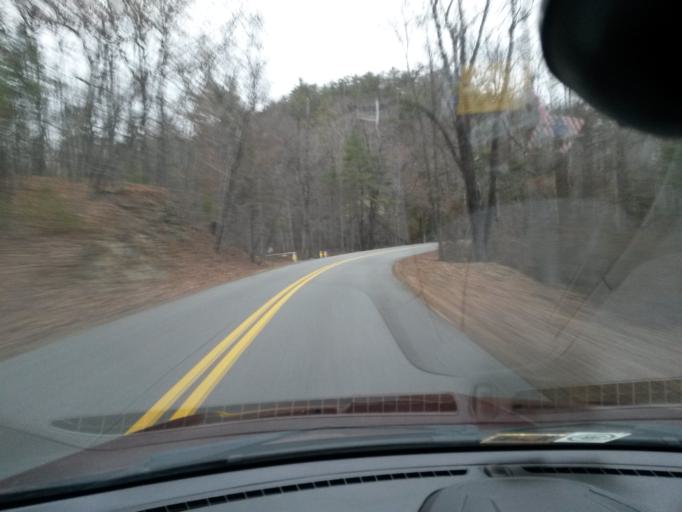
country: US
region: Virginia
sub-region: Alleghany County
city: Clifton Forge
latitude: 37.8612
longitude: -79.8153
